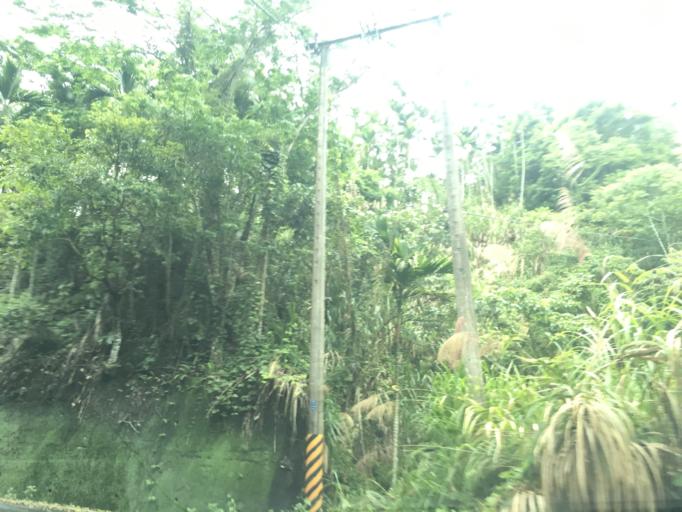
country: TW
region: Taiwan
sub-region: Yunlin
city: Douliu
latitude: 23.5626
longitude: 120.6456
